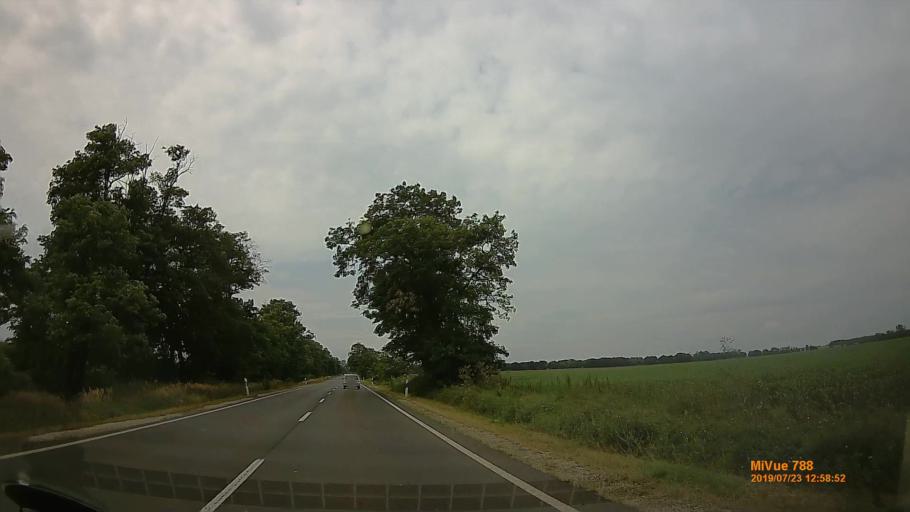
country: HU
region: Szabolcs-Szatmar-Bereg
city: Nagycserkesz
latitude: 47.9593
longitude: 21.4481
